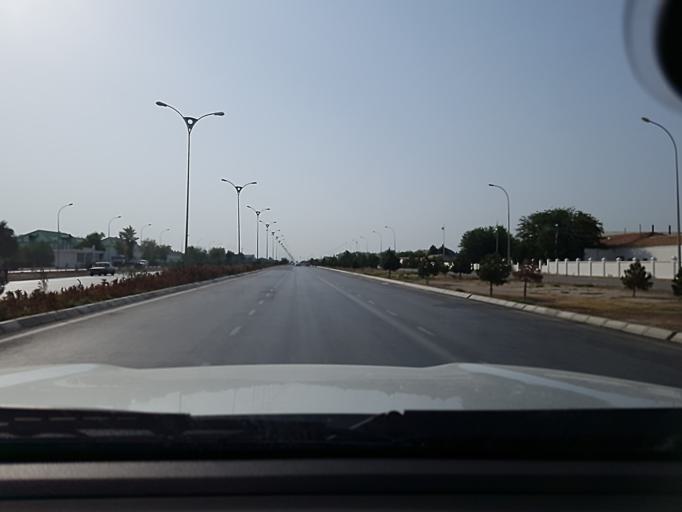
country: TM
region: Balkan
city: Balkanabat
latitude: 39.5027
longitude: 54.3606
